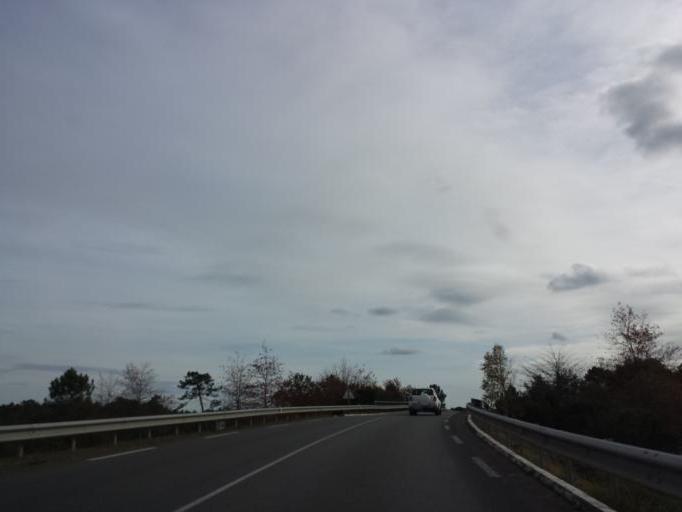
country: FR
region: Aquitaine
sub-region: Departement de la Gironde
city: Marcheprime
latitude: 44.7837
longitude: -0.9330
